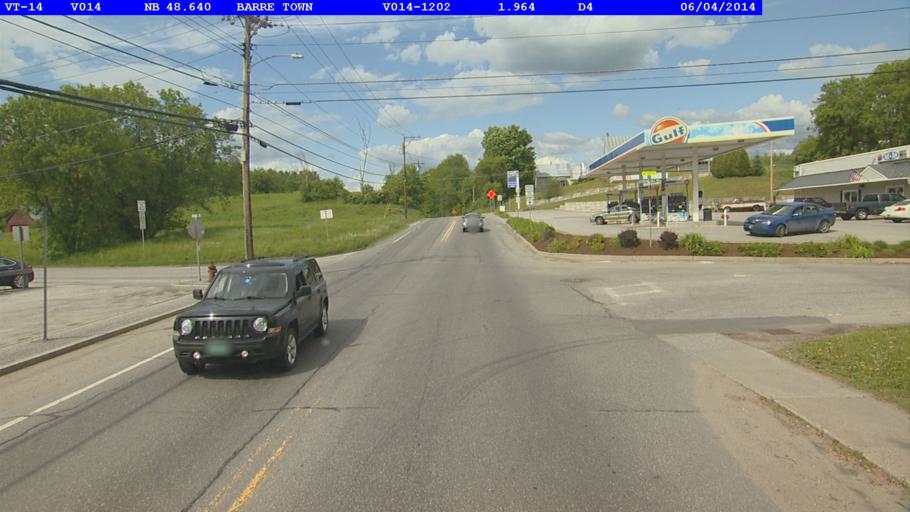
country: US
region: Vermont
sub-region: Washington County
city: South Barre
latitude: 44.1769
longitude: -72.5050
